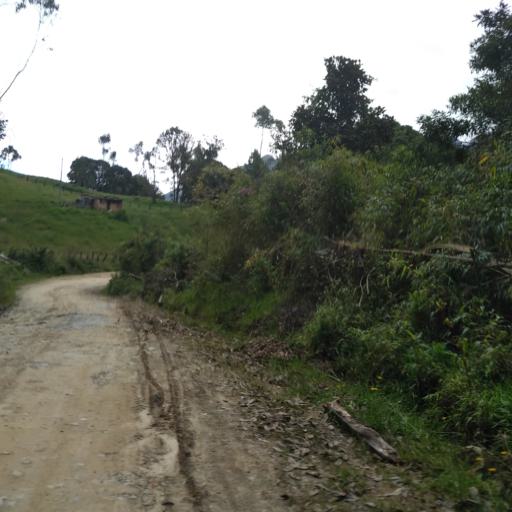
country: CO
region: Boyaca
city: Duitama
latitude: 5.9483
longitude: -73.1458
